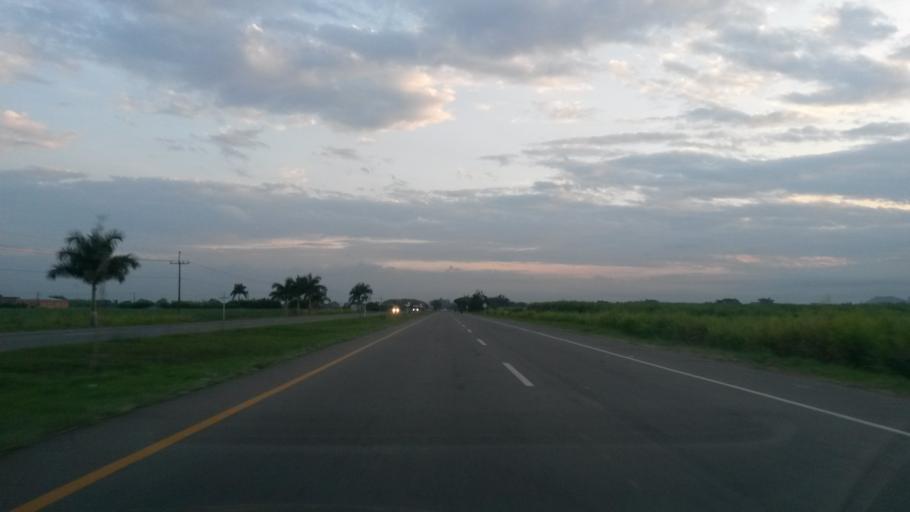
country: CO
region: Cauca
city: Santander de Quilichao
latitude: 3.0412
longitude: -76.4784
